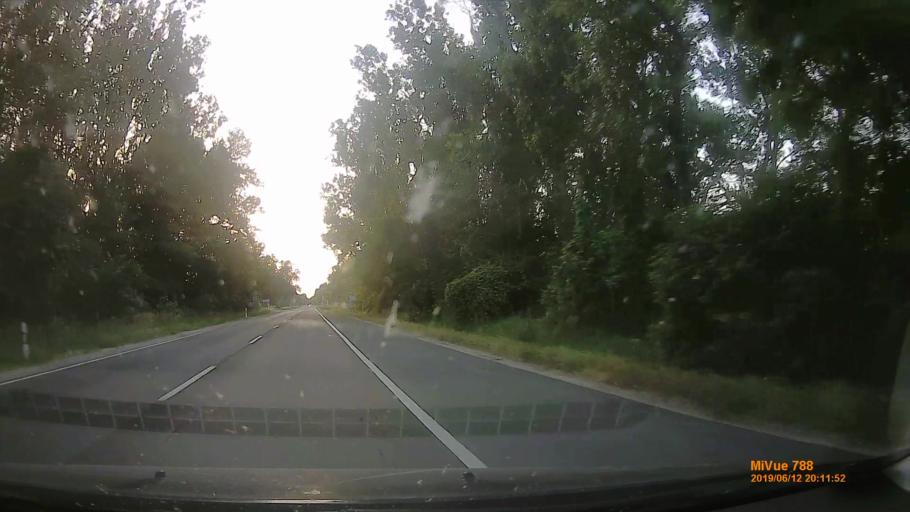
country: HU
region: Pest
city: Ocsa
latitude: 47.2810
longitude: 19.1984
